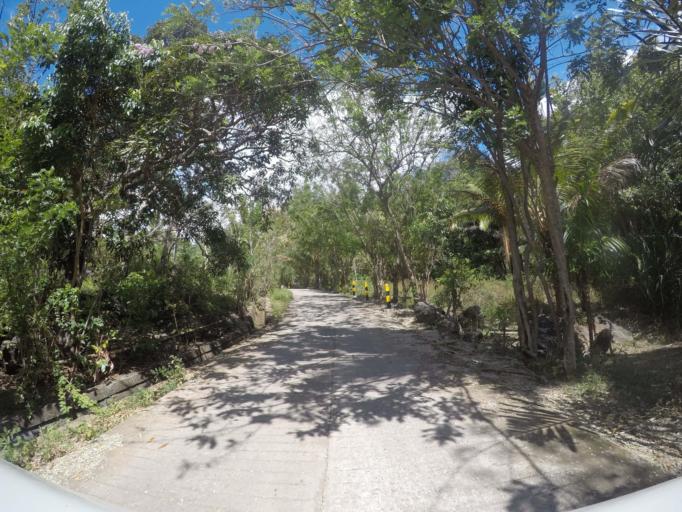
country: TL
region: Lautem
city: Lospalos
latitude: -8.5390
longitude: 126.8019
